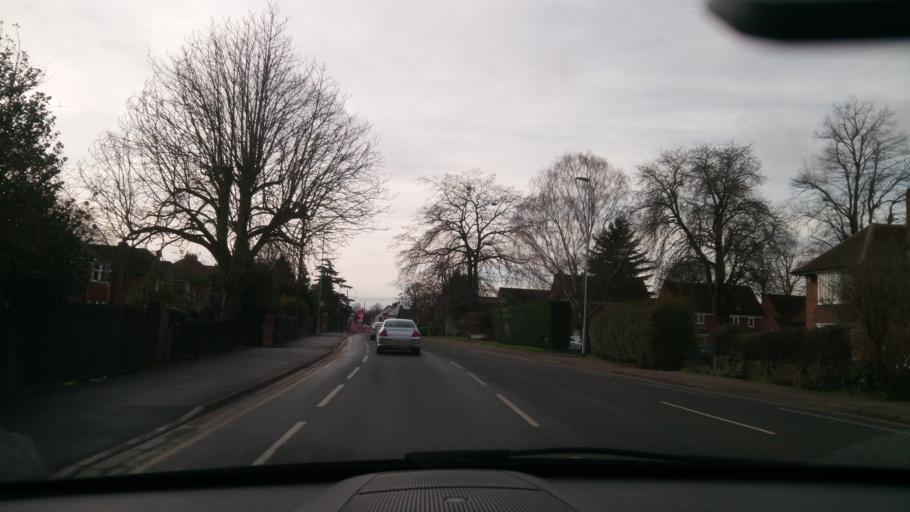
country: GB
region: England
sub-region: Peterborough
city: Peterborough
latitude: 52.5886
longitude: -0.2231
